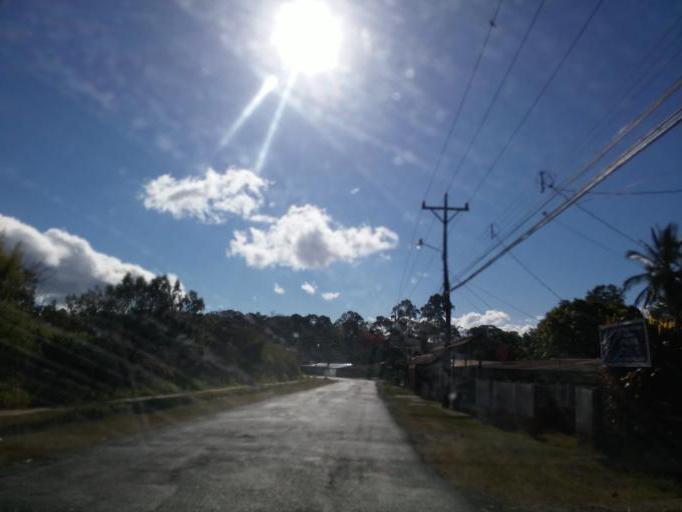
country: CR
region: Alajuela
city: Sabanilla
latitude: 10.0454
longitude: -84.2115
